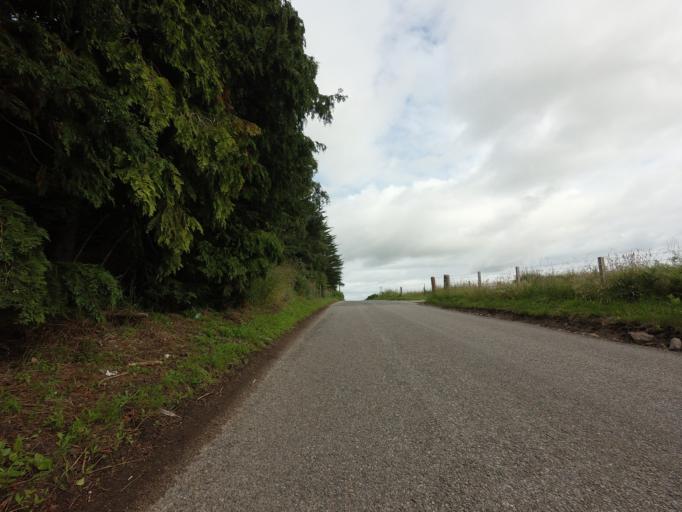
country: GB
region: Scotland
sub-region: Moray
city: Elgin
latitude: 57.6593
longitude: -3.3544
